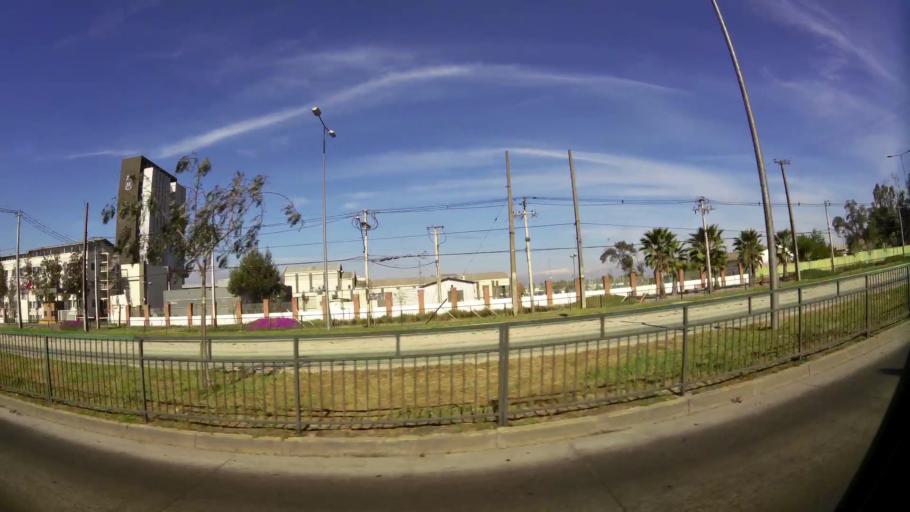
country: CL
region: Santiago Metropolitan
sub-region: Provincia de Santiago
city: Lo Prado
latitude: -33.4906
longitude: -70.7023
